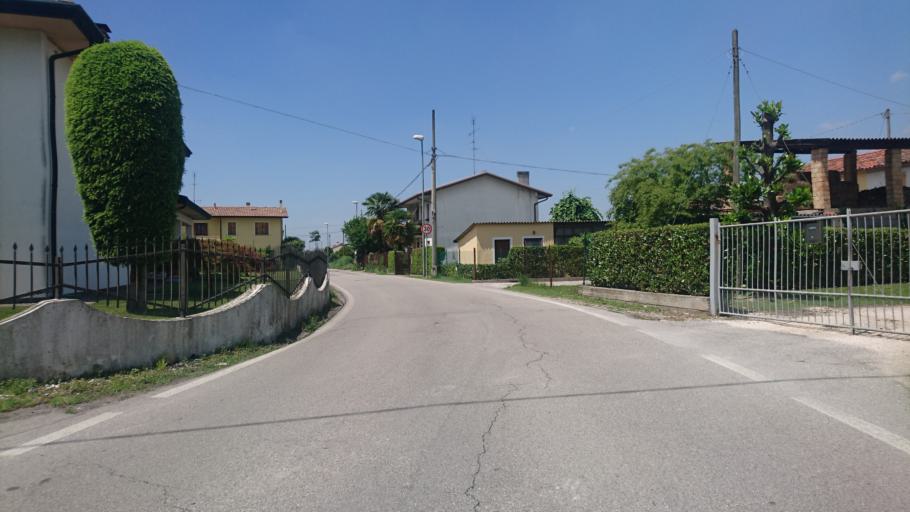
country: IT
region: Veneto
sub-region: Provincia di Venezia
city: Stra
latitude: 45.4183
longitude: 12.0141
